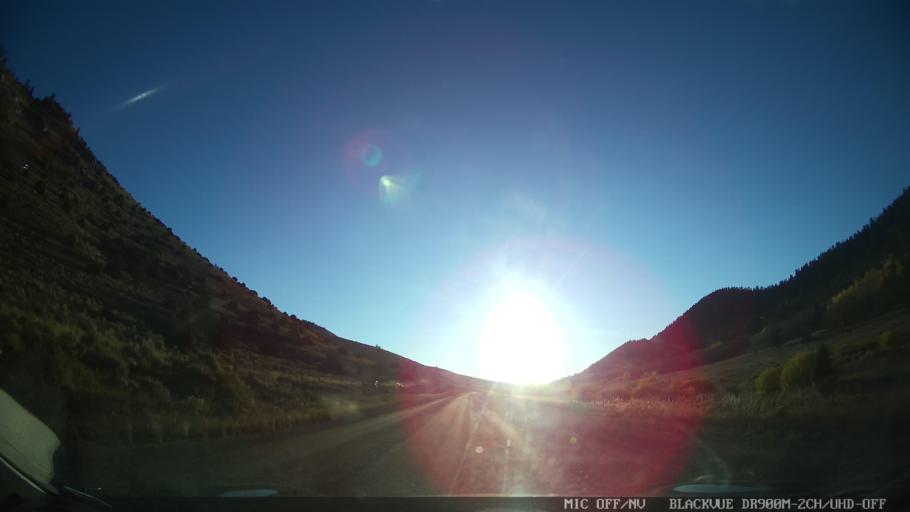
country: US
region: Colorado
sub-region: Grand County
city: Kremmling
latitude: 39.9935
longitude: -106.4682
